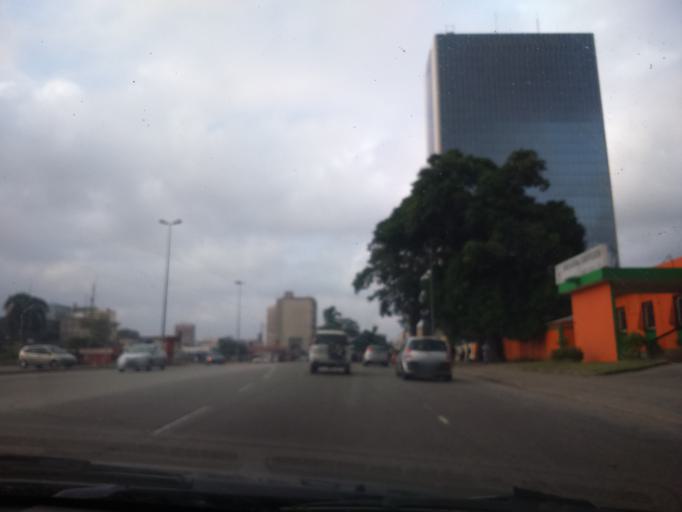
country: CI
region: Lagunes
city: Abidjan
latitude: 5.3329
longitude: -4.0217
